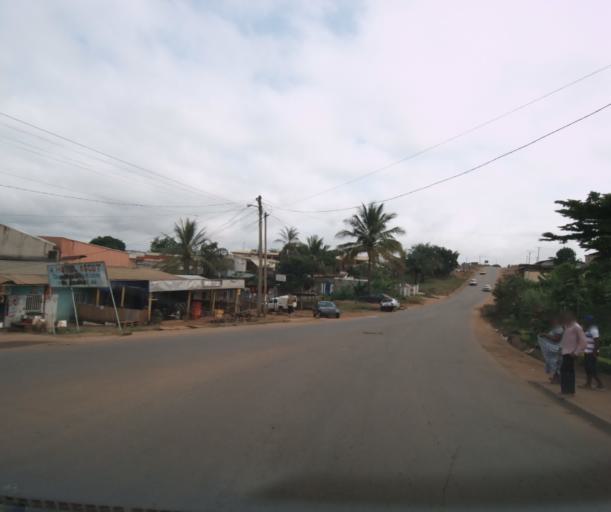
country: CM
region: Centre
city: Yaounde
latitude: 3.7997
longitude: 11.5222
